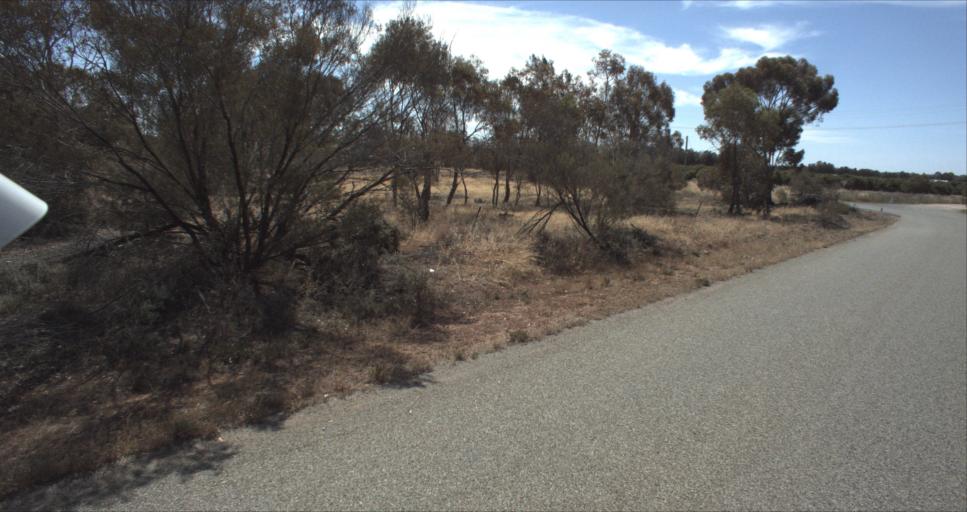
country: AU
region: New South Wales
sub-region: Leeton
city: Leeton
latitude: -34.6074
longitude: 146.4352
